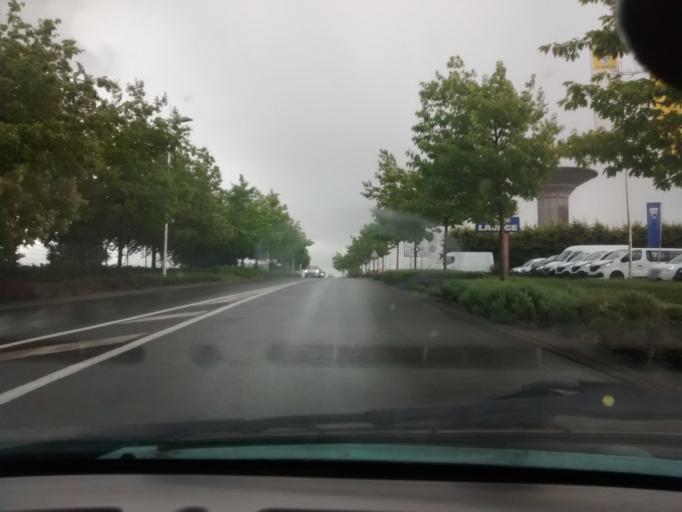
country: FR
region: Lower Normandy
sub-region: Departement de la Manche
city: Saint-Lo
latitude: 49.1054
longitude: -1.0679
